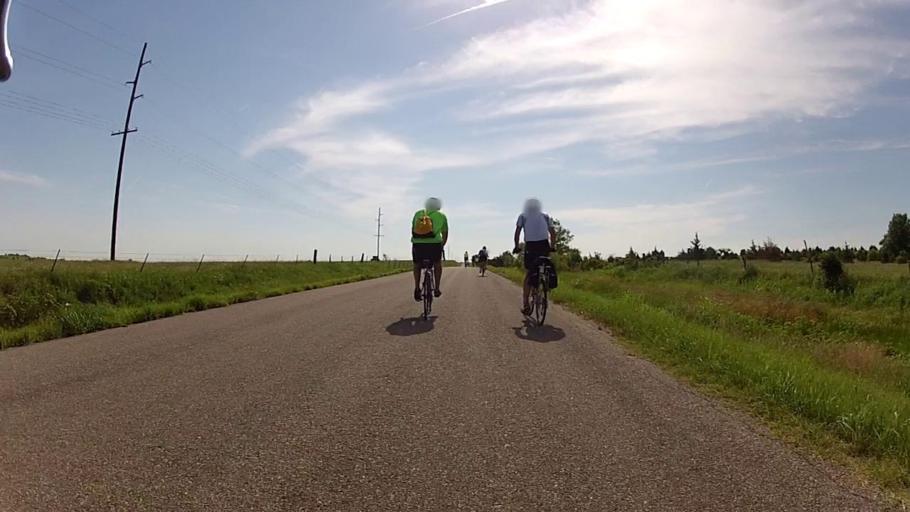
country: US
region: Kansas
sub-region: Cowley County
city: Winfield
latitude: 37.0710
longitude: -96.6531
